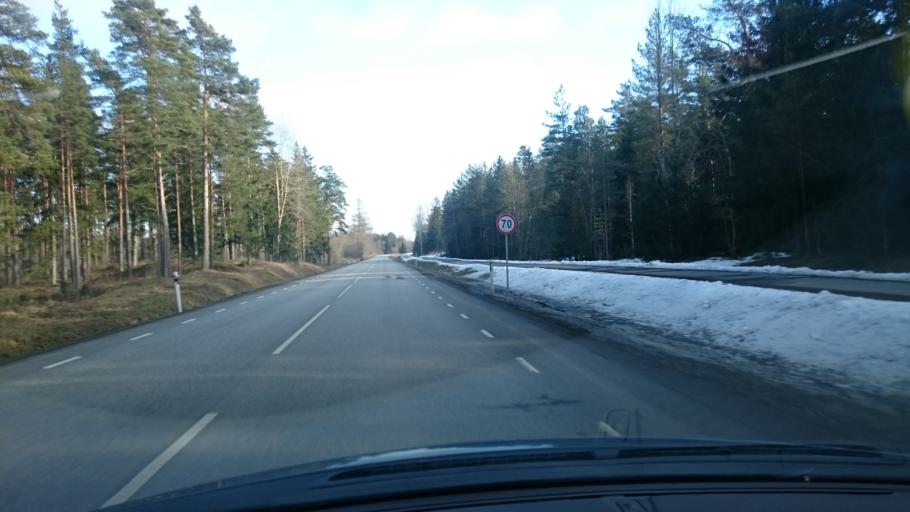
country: EE
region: Harju
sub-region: Kiili vald
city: Kiili
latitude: 59.3525
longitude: 24.7870
